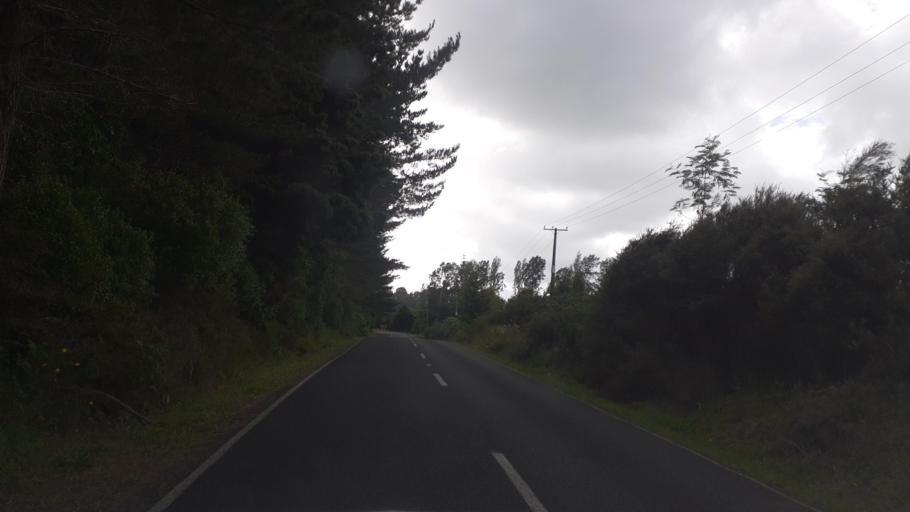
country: NZ
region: Northland
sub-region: Far North District
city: Kerikeri
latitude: -35.2252
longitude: 174.0198
